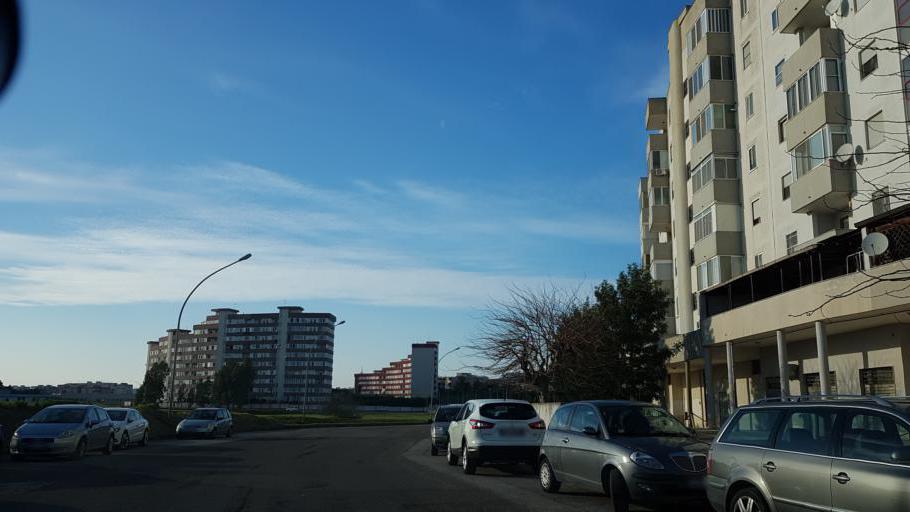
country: IT
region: Apulia
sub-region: Provincia di Brindisi
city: Brindisi
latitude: 40.6197
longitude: 17.9442
